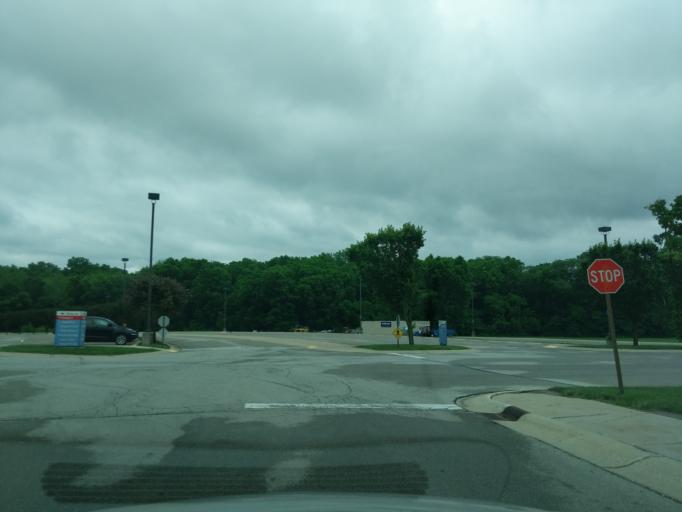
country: US
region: Indiana
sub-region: Hamilton County
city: Noblesville
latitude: 40.0443
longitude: -86.0245
